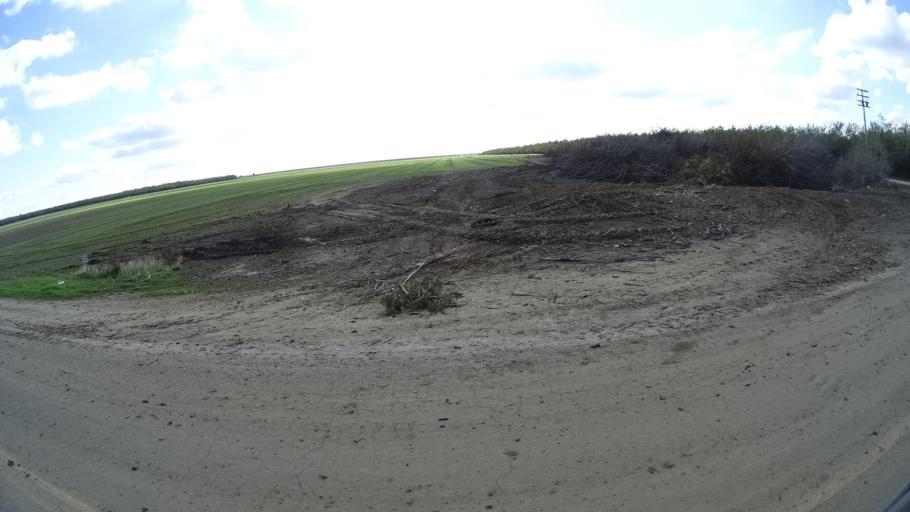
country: US
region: California
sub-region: Kern County
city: McFarland
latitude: 35.6814
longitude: -119.2671
